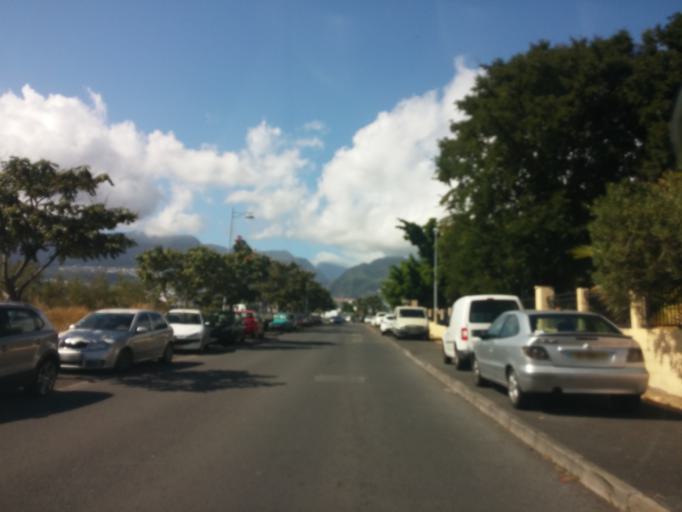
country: RE
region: Reunion
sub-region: Reunion
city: Le Port
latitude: -20.9543
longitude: 55.3061
